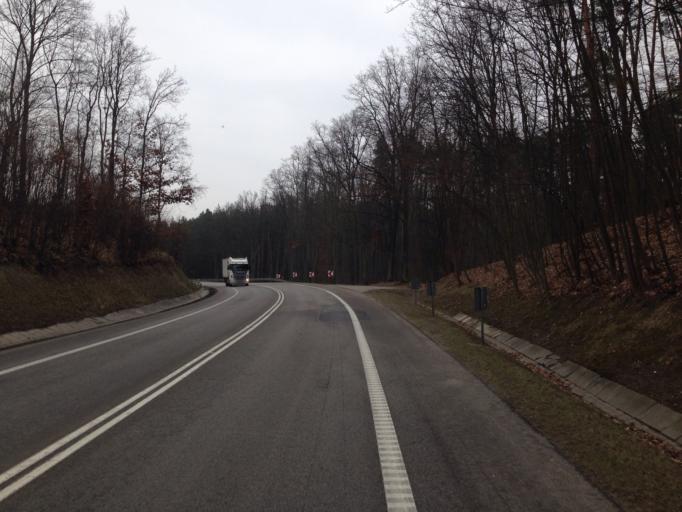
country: PL
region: Pomeranian Voivodeship
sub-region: Powiat starogardzki
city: Smetowo Graniczne
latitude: 53.7534
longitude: 18.7597
